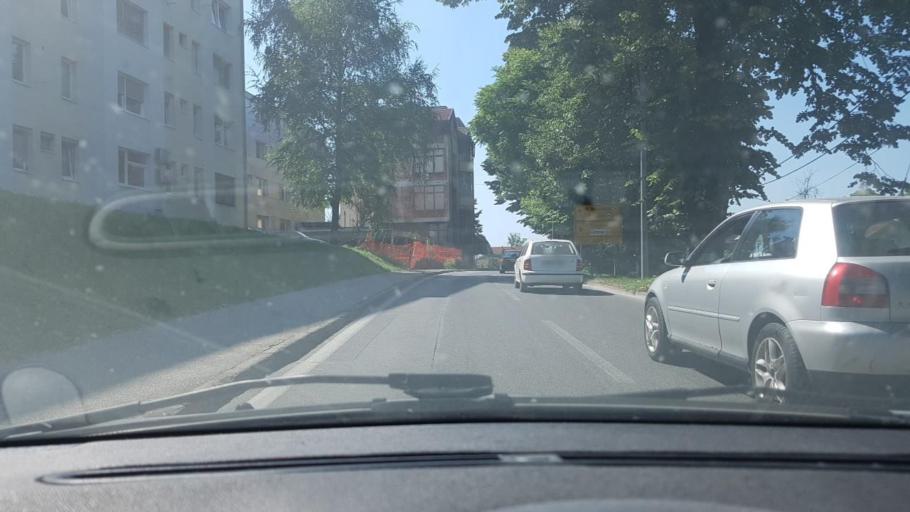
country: BA
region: Federation of Bosnia and Herzegovina
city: Bihac
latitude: 44.8164
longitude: 15.8704
